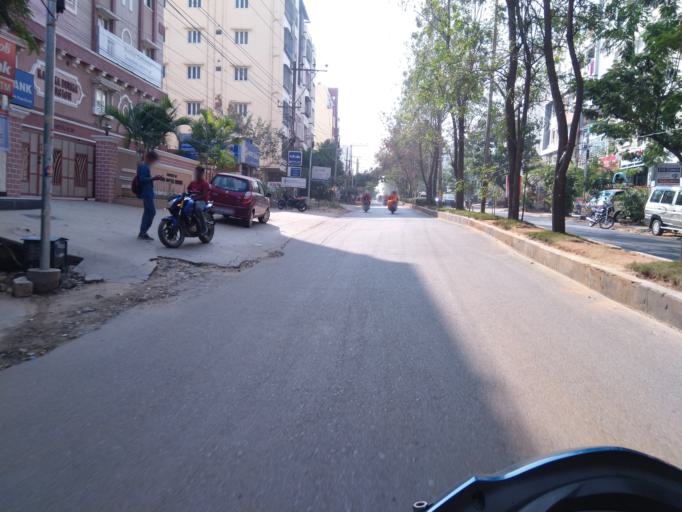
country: IN
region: Telangana
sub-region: Rangareddi
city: Kukatpalli
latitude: 17.4798
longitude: 78.3943
